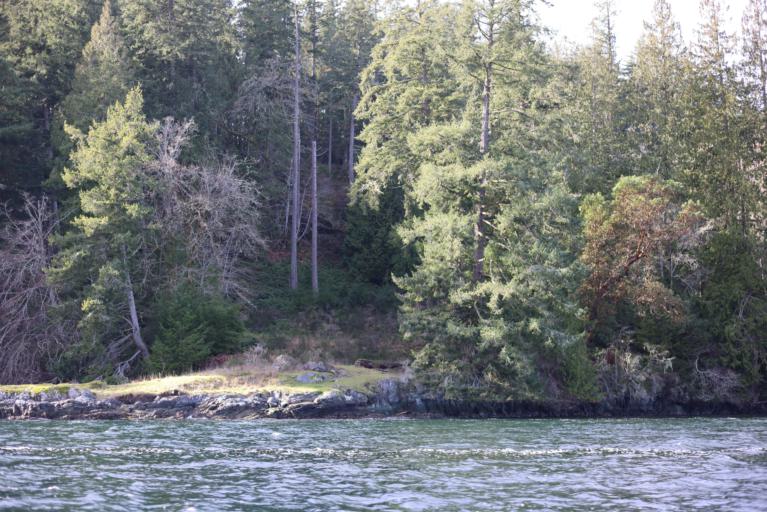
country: CA
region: British Columbia
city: North Cowichan
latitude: 48.7835
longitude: -123.5584
